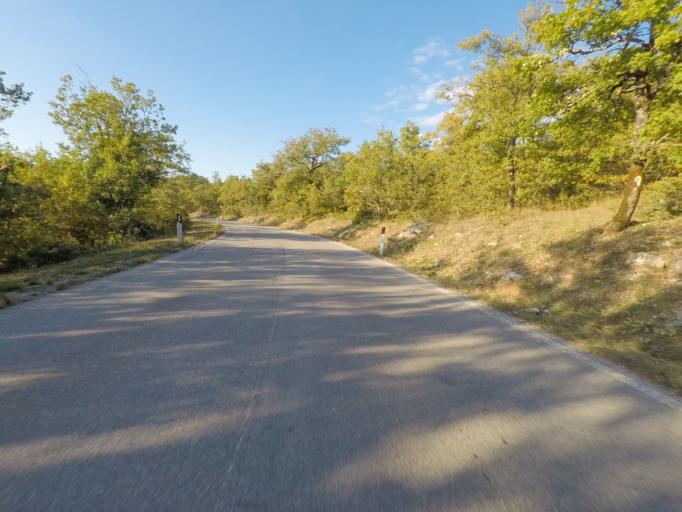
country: IT
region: Tuscany
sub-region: Provincia di Siena
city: Radda in Chianti
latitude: 43.4533
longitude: 11.3862
